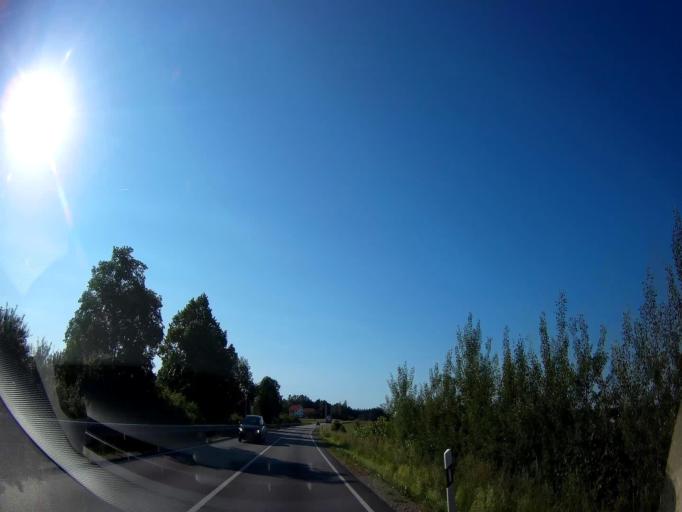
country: DE
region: Bavaria
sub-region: Lower Bavaria
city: Wurmannsquick
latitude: 48.3686
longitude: 12.7855
